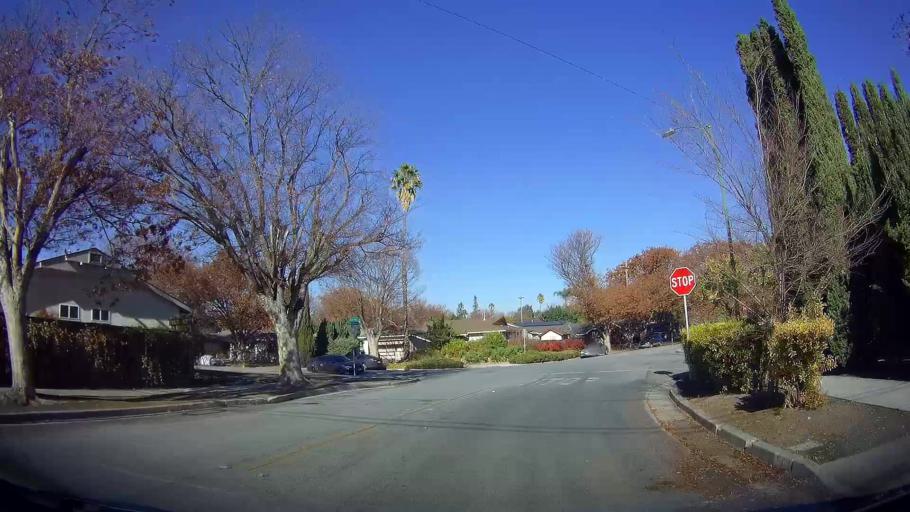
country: US
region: California
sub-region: Santa Clara County
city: Seven Trees
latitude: 37.2879
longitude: -121.8771
